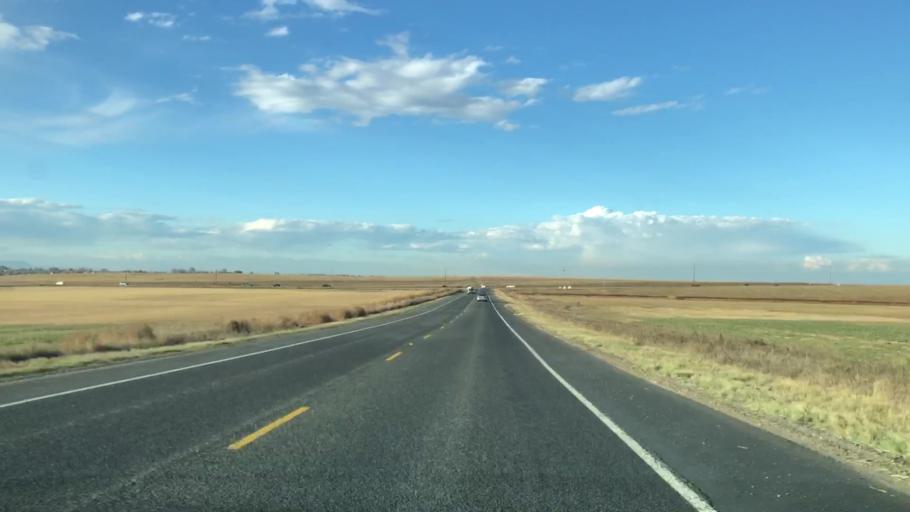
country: US
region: Colorado
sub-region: Larimer County
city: Loveland
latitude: 40.4761
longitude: -105.0202
